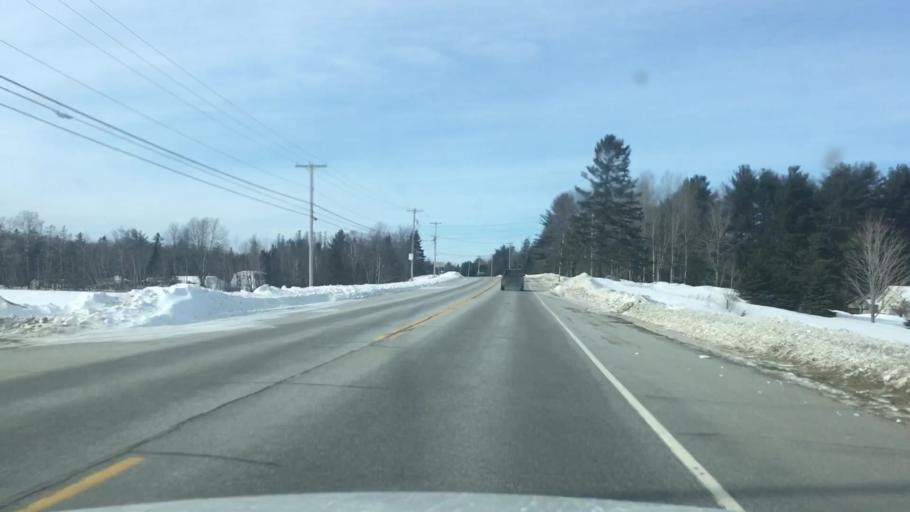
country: US
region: Maine
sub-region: Penobscot County
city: Kenduskeag
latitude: 44.9527
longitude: -68.9492
